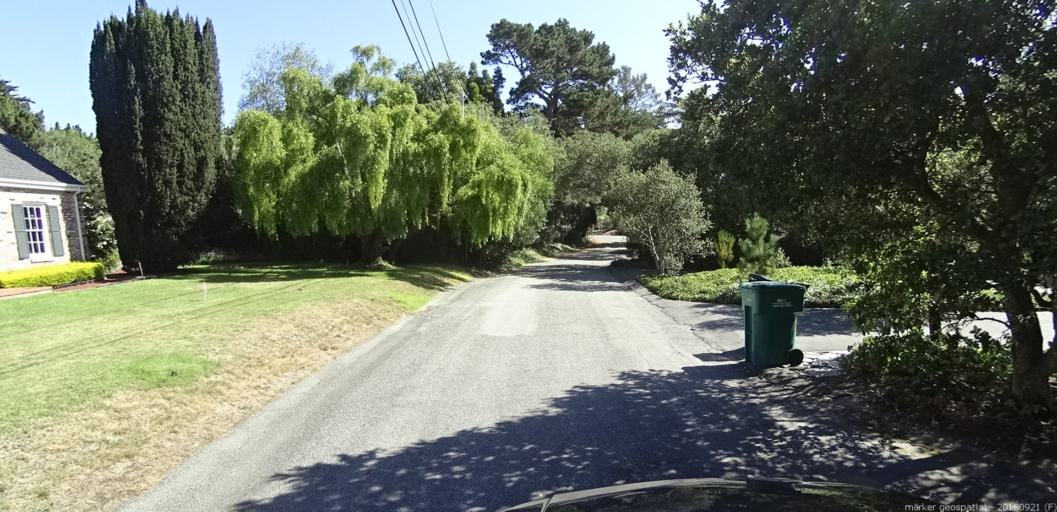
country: US
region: California
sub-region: Monterey County
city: Carmel-by-the-Sea
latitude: 36.5562
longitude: -121.9142
